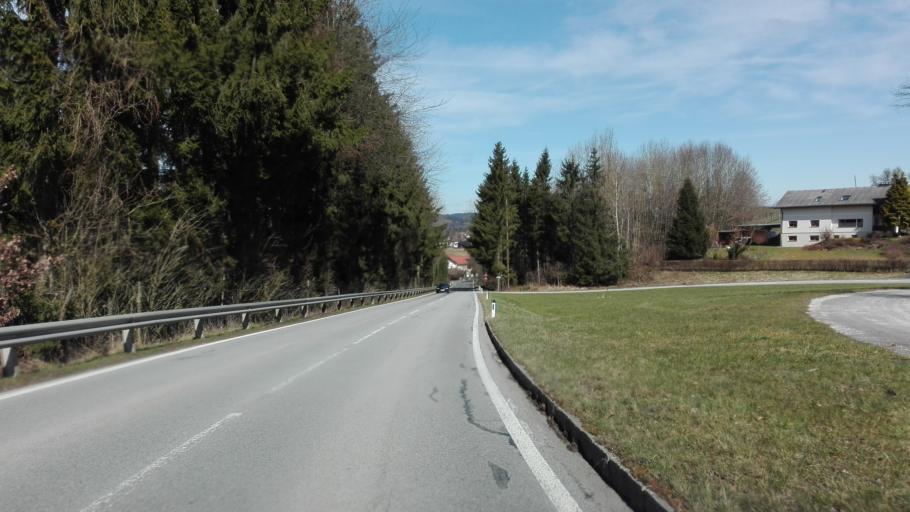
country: AT
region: Upper Austria
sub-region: Politischer Bezirk Scharding
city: Sankt Marienkirchen bei Schaerding
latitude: 48.3453
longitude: 13.6333
